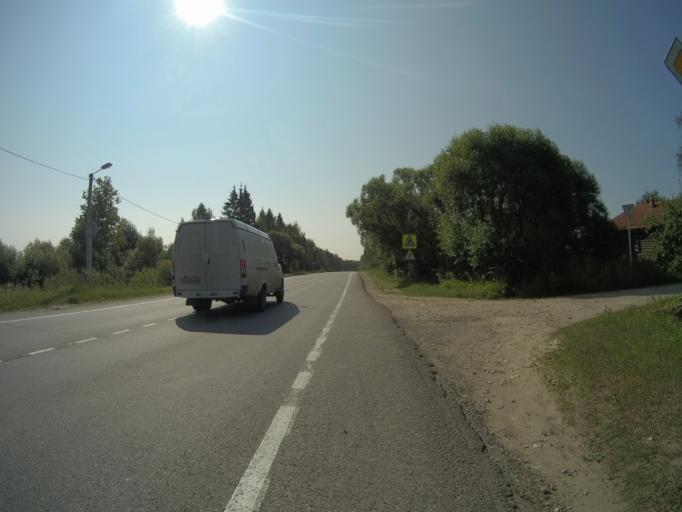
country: RU
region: Vladimir
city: Golovino
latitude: 55.9289
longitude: 40.5963
